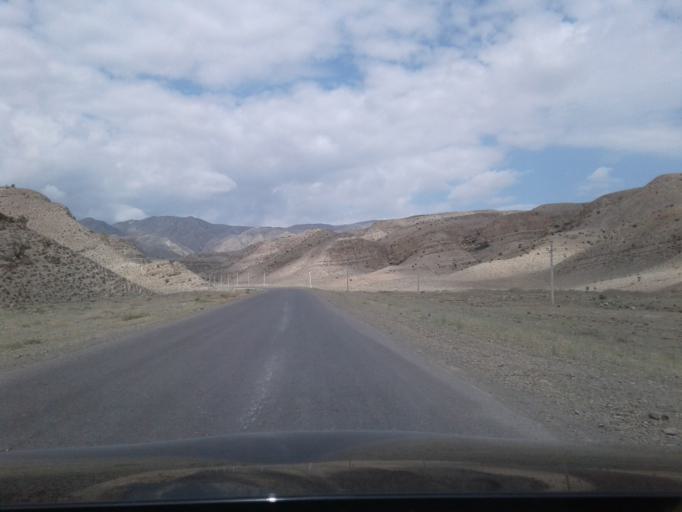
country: TM
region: Ahal
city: Baharly
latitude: 38.5010
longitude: 57.1073
